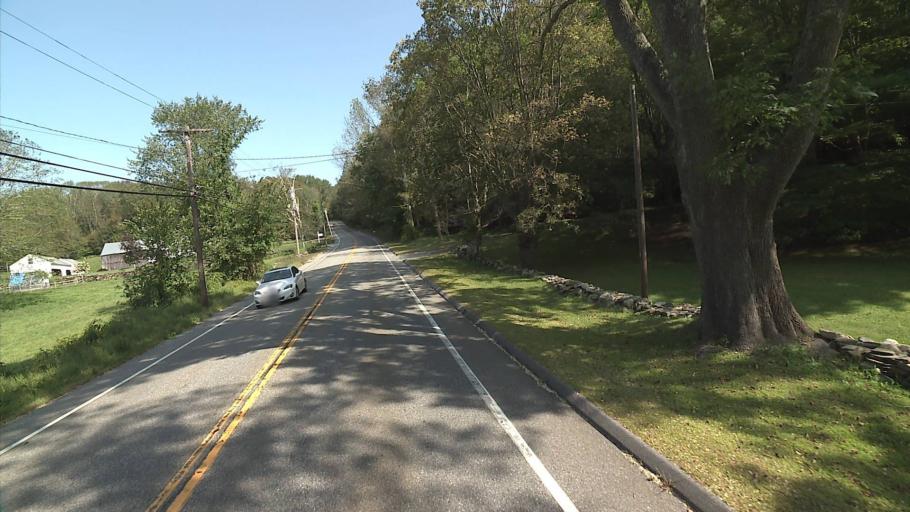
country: US
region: Connecticut
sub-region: Windham County
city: South Woodstock
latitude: 41.8734
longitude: -71.9621
